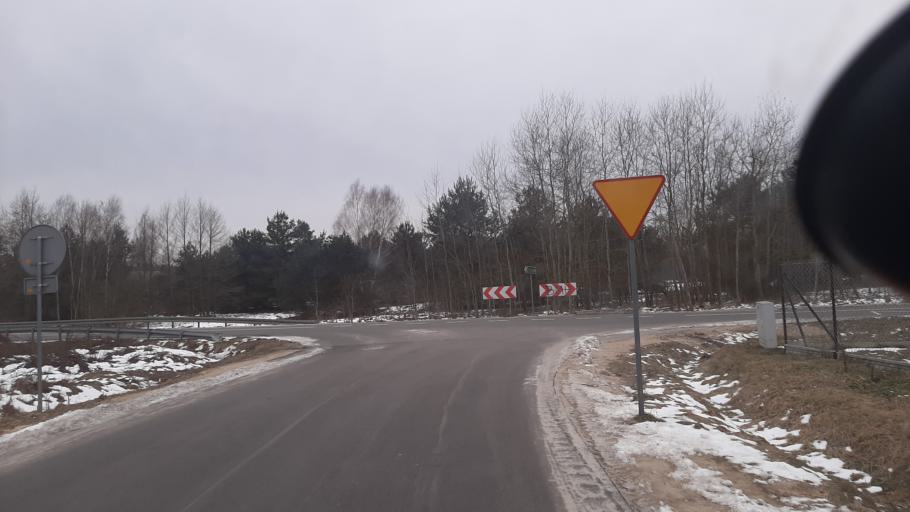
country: PL
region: Lublin Voivodeship
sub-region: Powiat lubartowski
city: Kamionka
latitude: 51.4858
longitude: 22.4479
